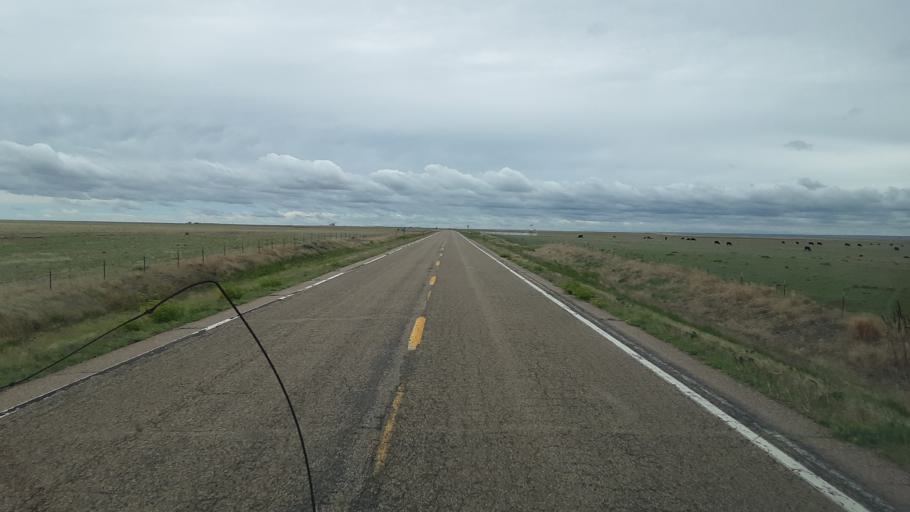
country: US
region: Colorado
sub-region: Lincoln County
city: Limon
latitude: 38.8522
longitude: -103.7849
